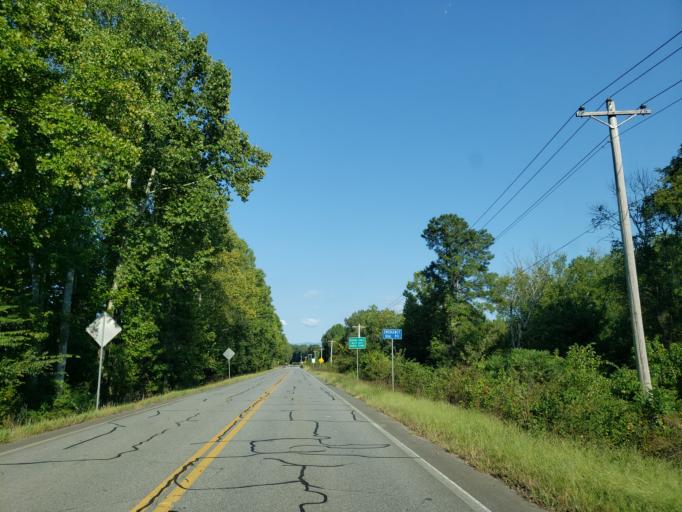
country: US
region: Georgia
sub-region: Whitfield County
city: Varnell
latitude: 34.9213
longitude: -84.8406
